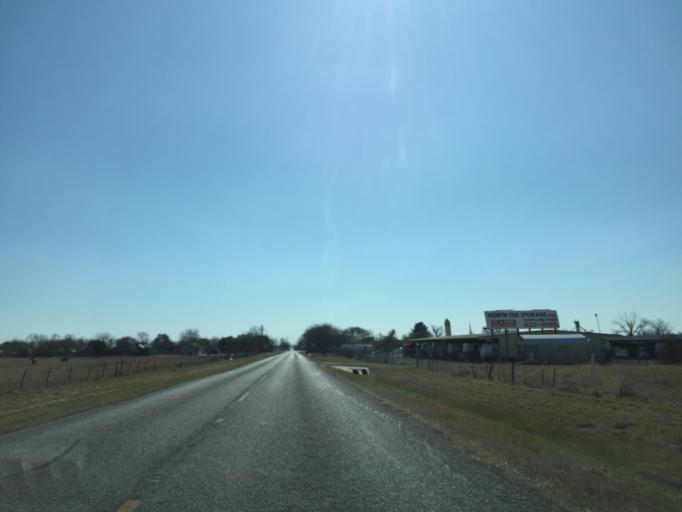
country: US
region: Texas
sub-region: Williamson County
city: Georgetown
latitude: 30.6791
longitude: -97.5878
